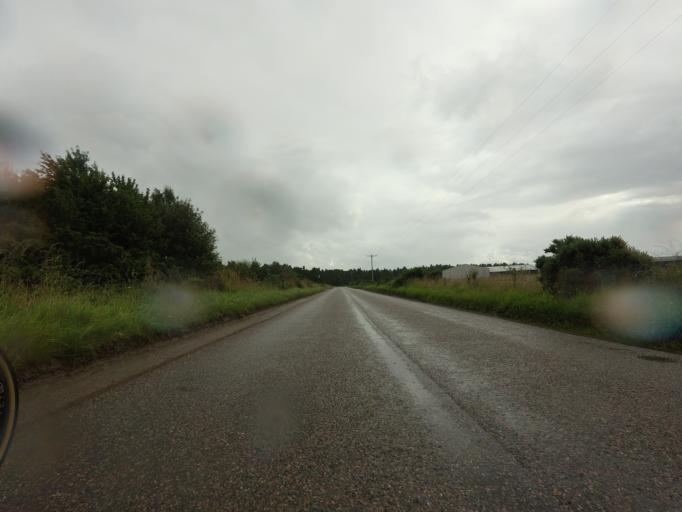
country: GB
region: Scotland
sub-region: Moray
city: Fochabers
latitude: 57.6582
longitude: -3.0578
